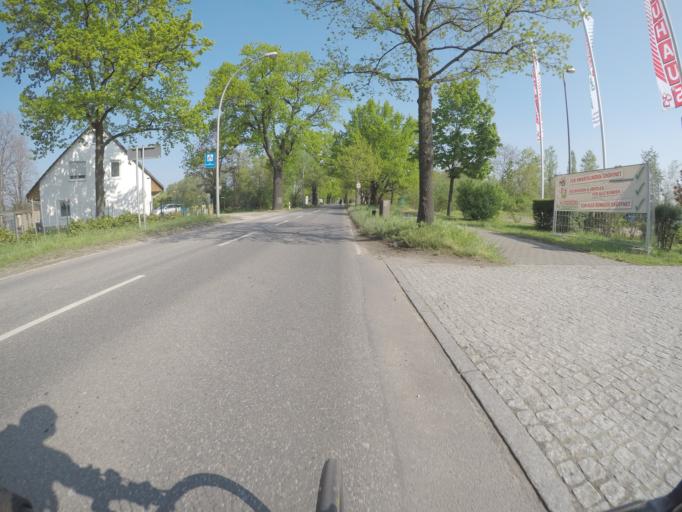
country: DE
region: Berlin
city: Buchholz
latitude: 52.6152
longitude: 13.4318
